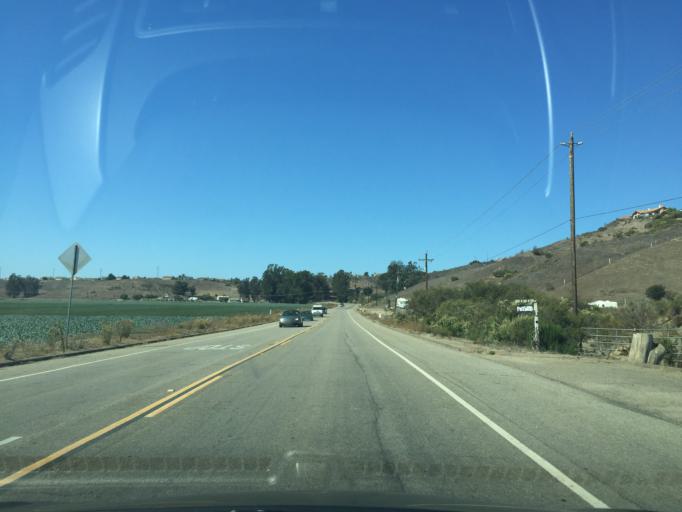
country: US
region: California
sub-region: Santa Barbara County
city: Mission Hills
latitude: 34.6755
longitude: -120.4415
